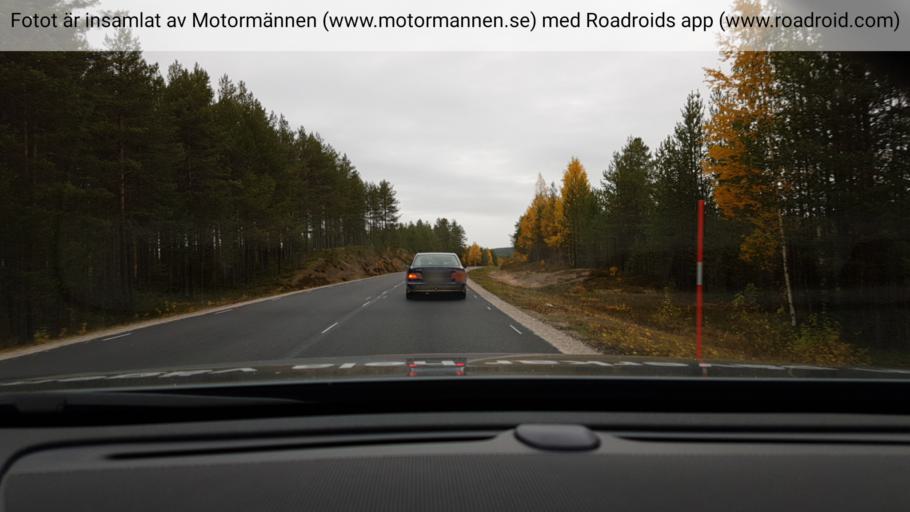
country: SE
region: Norrbotten
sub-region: Overkalix Kommun
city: OEverkalix
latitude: 66.4452
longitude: 22.7862
